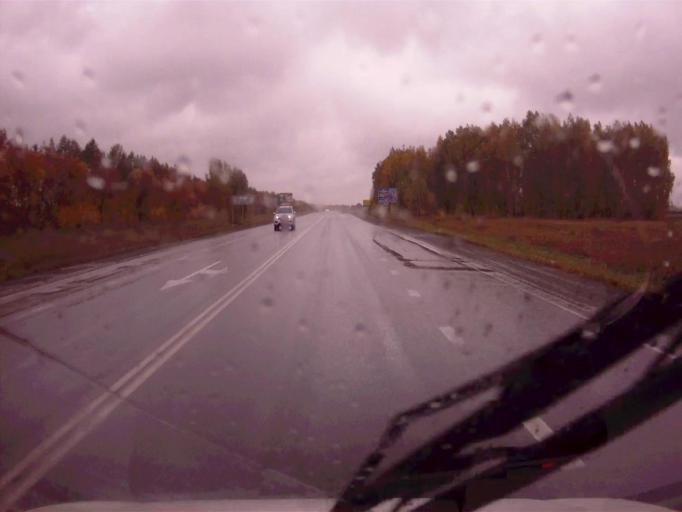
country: RU
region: Chelyabinsk
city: Roshchino
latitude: 55.3958
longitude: 61.0962
